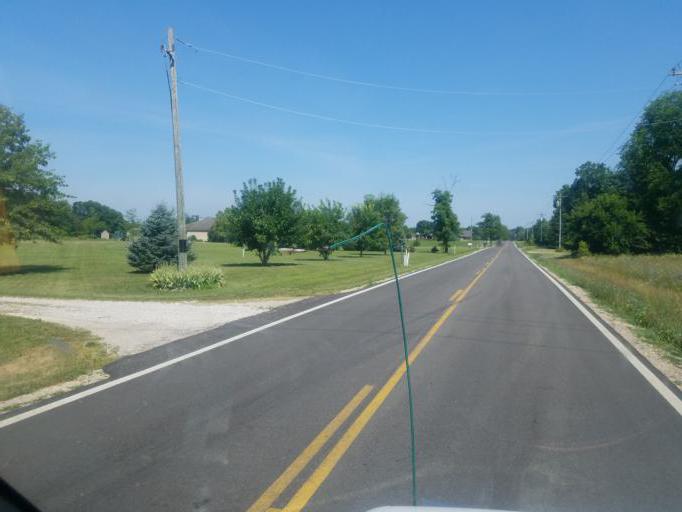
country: US
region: Ohio
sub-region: Union County
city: Marysville
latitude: 40.2099
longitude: -83.4485
